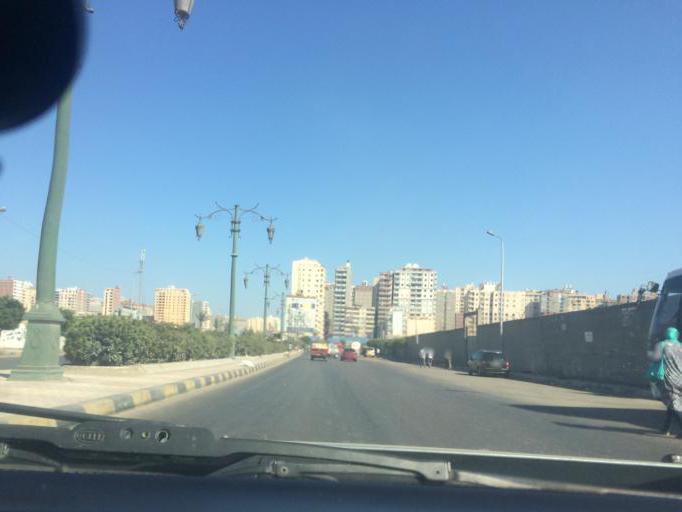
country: EG
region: Alexandria
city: Alexandria
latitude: 31.2590
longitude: 30.0128
